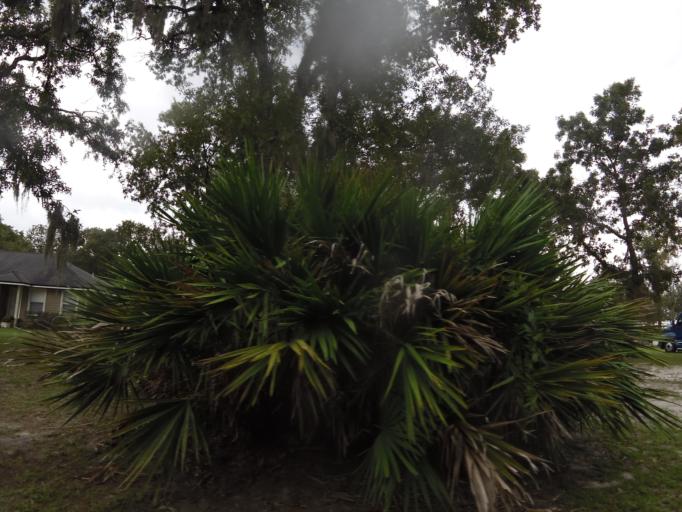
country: US
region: Florida
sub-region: Clay County
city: Middleburg
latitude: 30.1068
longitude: -81.9582
